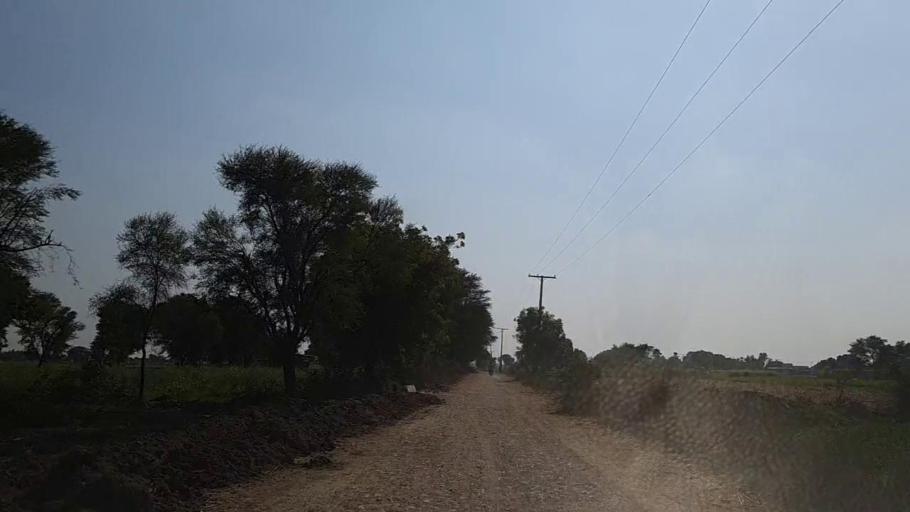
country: PK
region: Sindh
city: Daur
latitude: 26.4830
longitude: 68.2498
